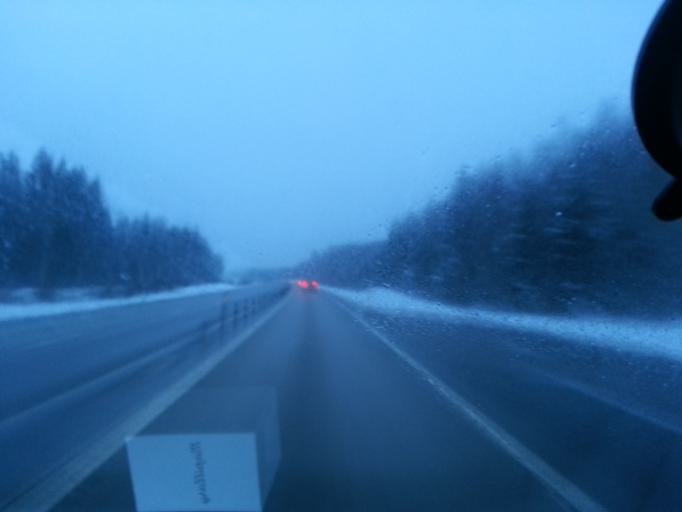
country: SE
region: Kronoberg
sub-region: Ljungby Kommun
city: Lagan
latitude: 57.0049
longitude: 14.0365
